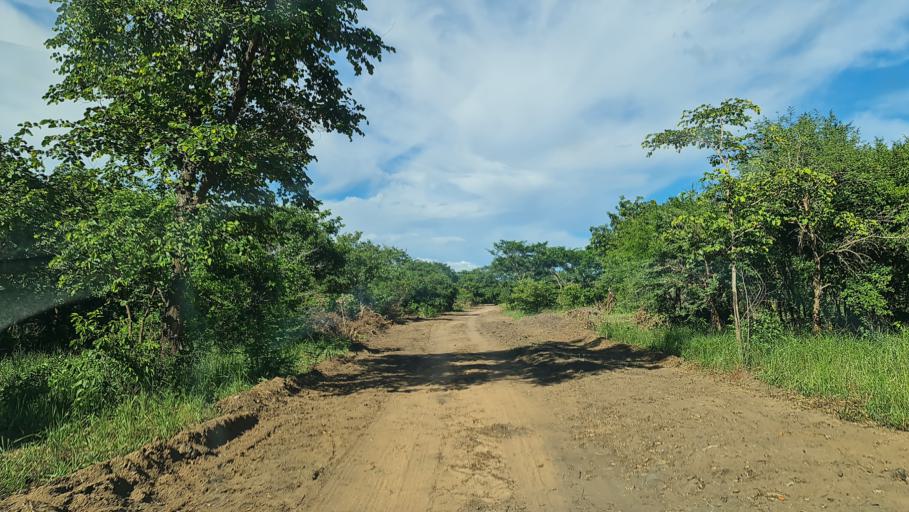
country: MZ
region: Nampula
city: Antonio Enes
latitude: -15.5116
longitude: 40.1324
